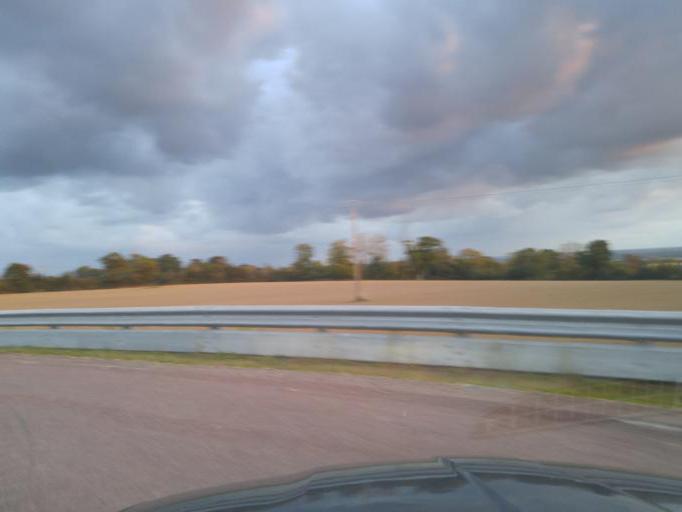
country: FR
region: Lower Normandy
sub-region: Departement du Calvados
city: Grandcamp-Maisy
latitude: 49.3402
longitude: -0.9803
